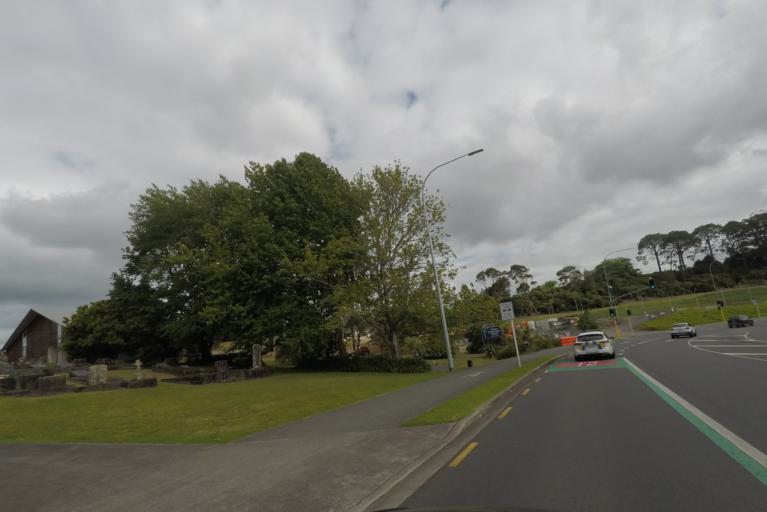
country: NZ
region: Auckland
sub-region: Auckland
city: Rothesay Bay
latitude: -36.7297
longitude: 174.6972
